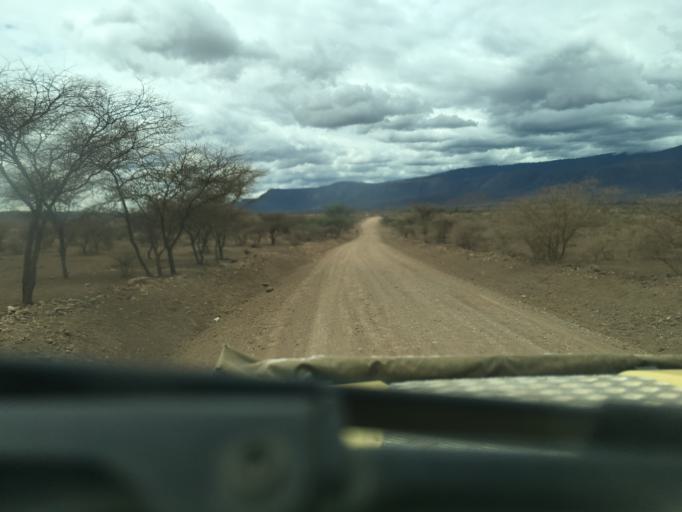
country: TZ
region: Arusha
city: Mto wa Mbu
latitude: -3.0986
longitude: 36.0162
